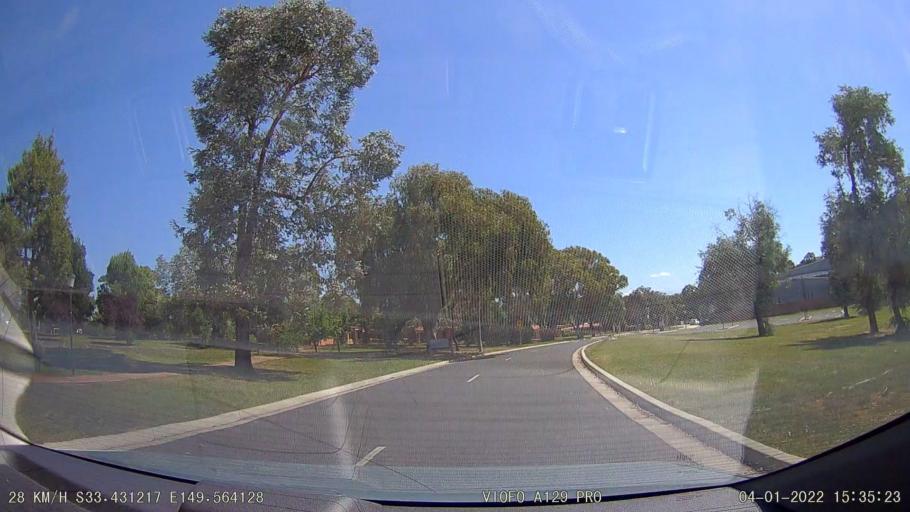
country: AU
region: New South Wales
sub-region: Bathurst Regional
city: Bathurst
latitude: -33.4311
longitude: 149.5642
